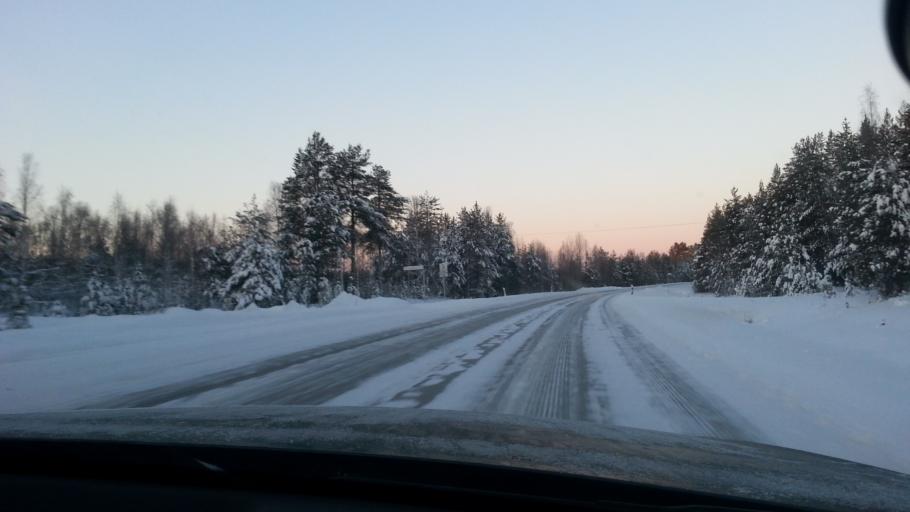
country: FI
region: Lapland
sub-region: Tunturi-Lappi
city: Kittilae
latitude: 67.0645
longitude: 25.0802
